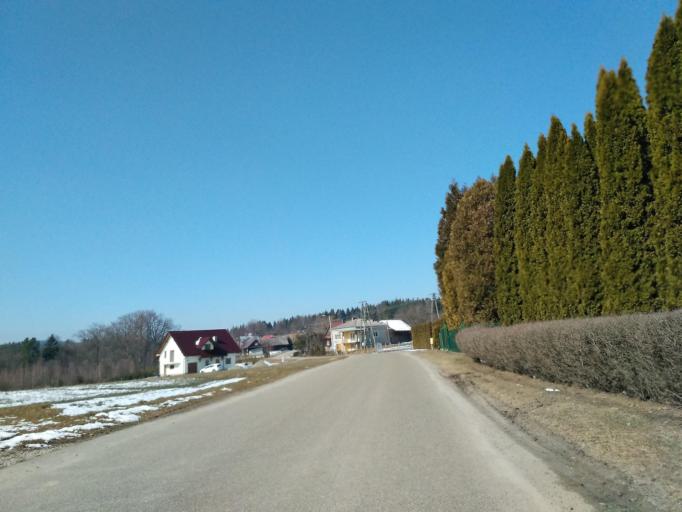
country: PL
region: Subcarpathian Voivodeship
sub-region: Powiat brzozowski
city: Jasienica Rosielna
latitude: 49.7707
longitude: 21.9185
